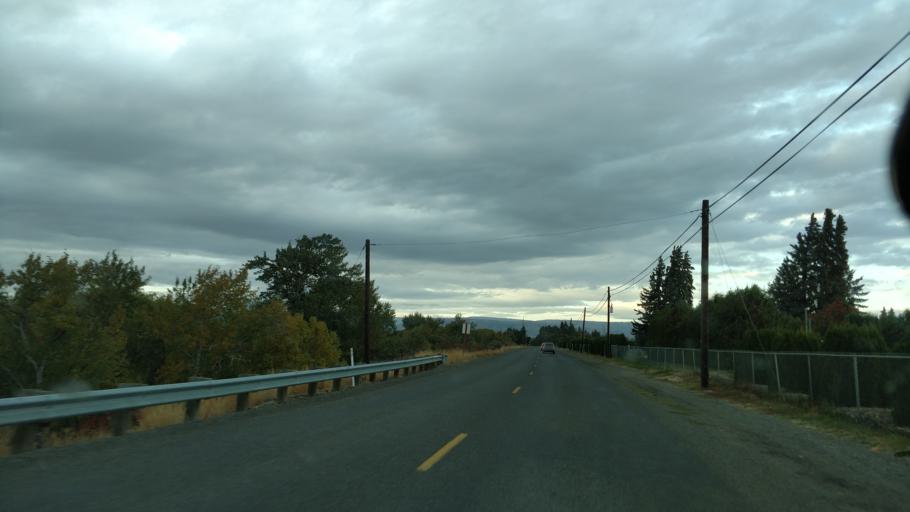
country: US
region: Washington
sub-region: Kittitas County
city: Ellensburg
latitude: 47.0099
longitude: -120.5228
